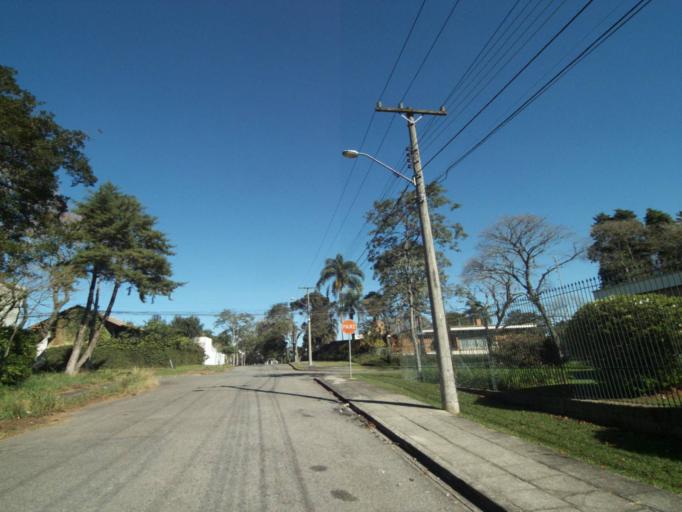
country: BR
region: Parana
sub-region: Curitiba
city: Curitiba
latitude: -25.4203
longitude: -49.2406
